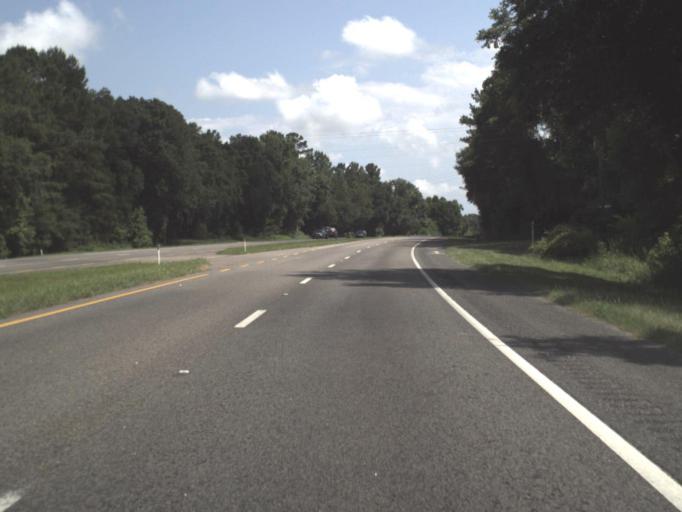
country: US
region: Florida
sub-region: Alachua County
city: Gainesville
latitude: 29.5295
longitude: -82.3085
